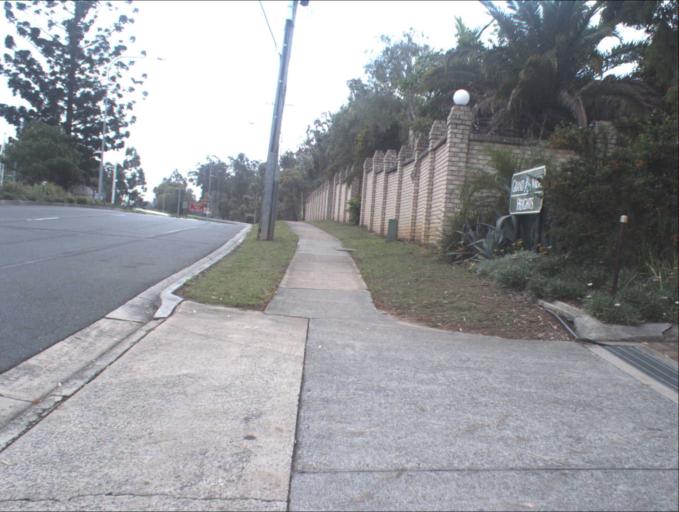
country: AU
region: Queensland
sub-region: Brisbane
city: Sunnybank Hills
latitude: -27.6548
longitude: 153.0406
